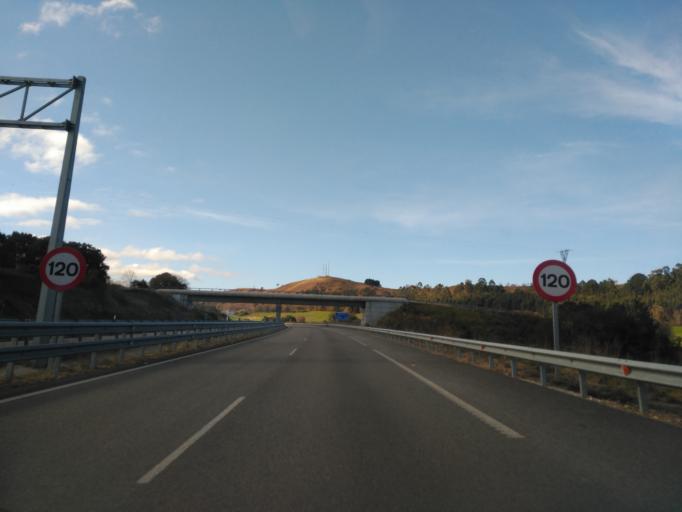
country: ES
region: Asturias
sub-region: Province of Asturias
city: Llanes
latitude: 43.4010
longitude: -4.7219
